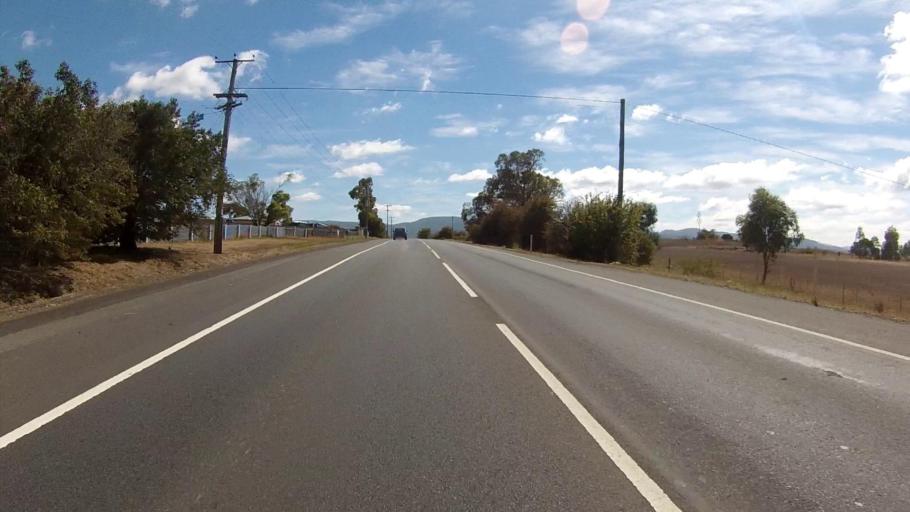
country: AU
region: Tasmania
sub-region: Brighton
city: Bridgewater
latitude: -42.7112
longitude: 147.2452
